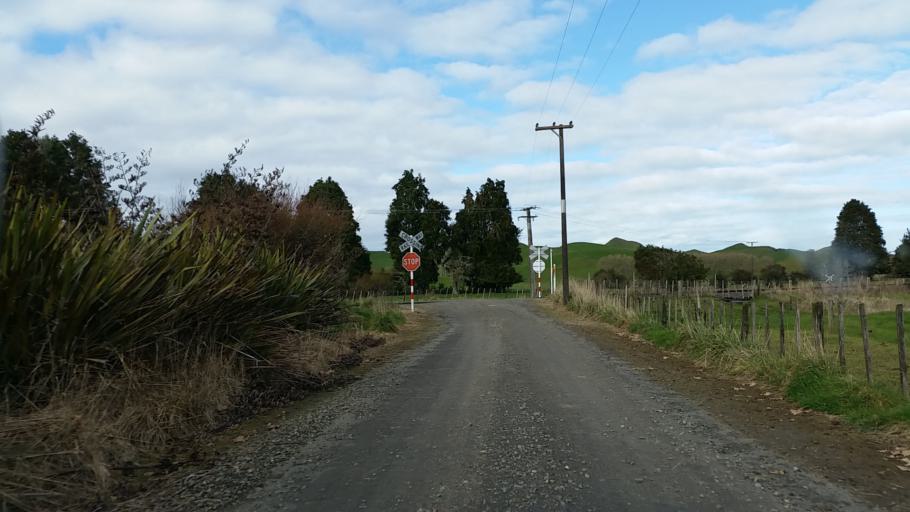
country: NZ
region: Taranaki
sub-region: South Taranaki District
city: Eltham
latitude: -39.2341
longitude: 174.5202
